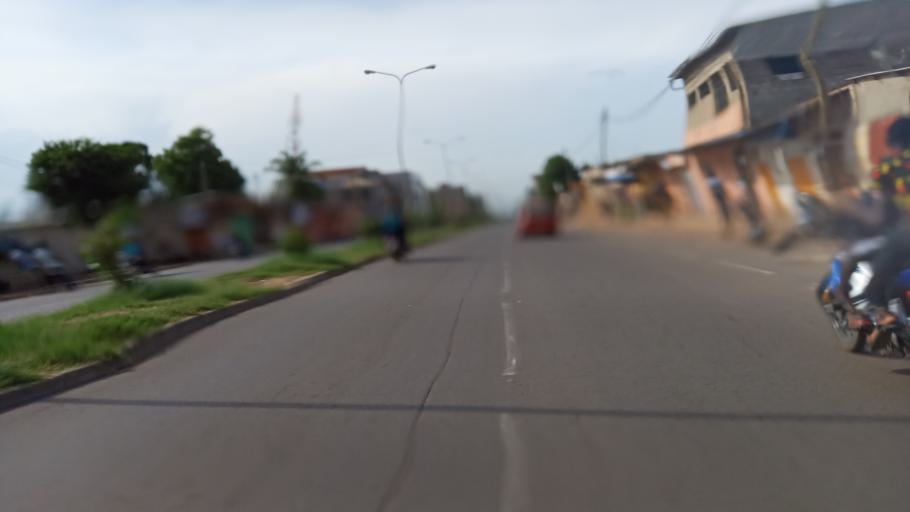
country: TG
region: Maritime
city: Lome
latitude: 6.1709
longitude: 1.2672
